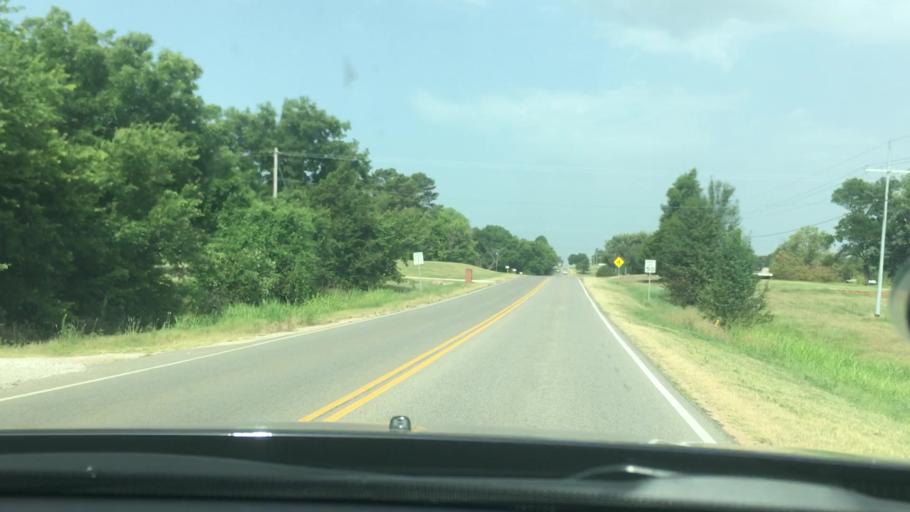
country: US
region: Oklahoma
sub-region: Pontotoc County
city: Ada
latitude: 34.7821
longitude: -96.7642
